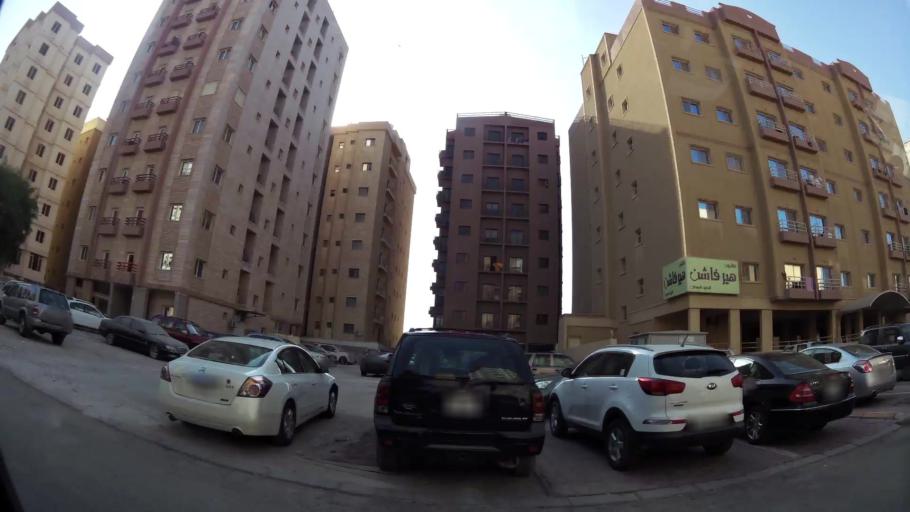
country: KW
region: Muhafazat Hawalli
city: As Salimiyah
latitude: 29.3431
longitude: 48.0936
